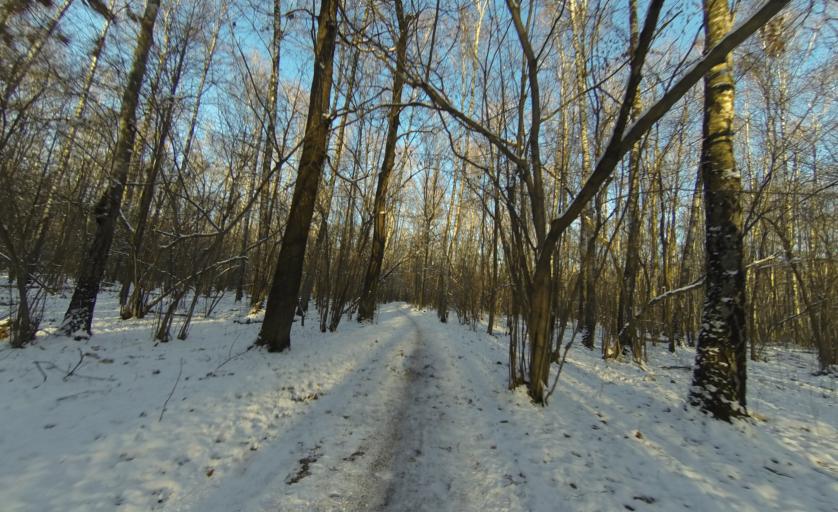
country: RU
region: Moscow
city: Rostokino
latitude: 55.8276
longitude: 37.6901
